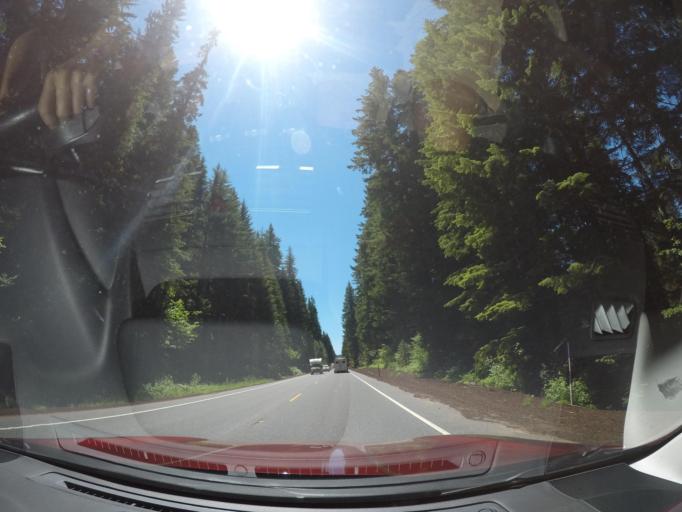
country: US
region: Oregon
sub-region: Deschutes County
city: Sisters
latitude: 44.5330
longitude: -121.9948
